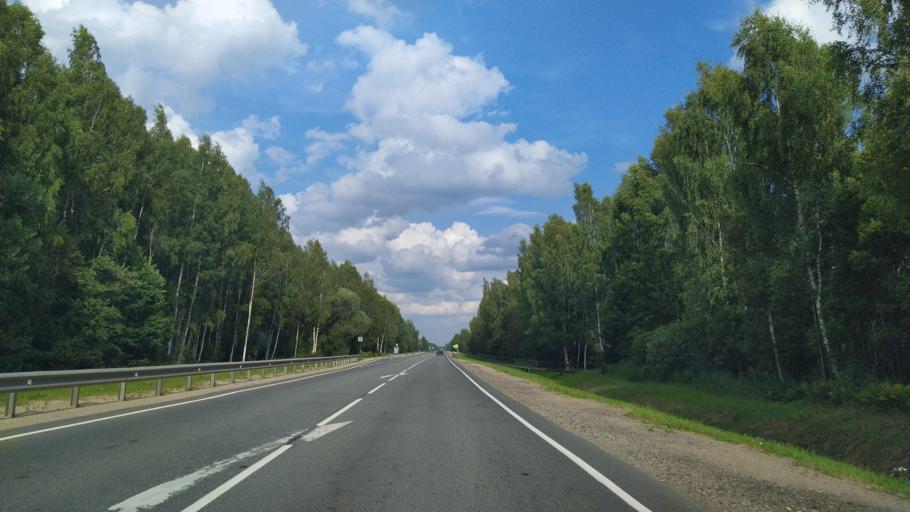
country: RU
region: Novgorod
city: Sol'tsy
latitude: 58.1653
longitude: 30.4643
